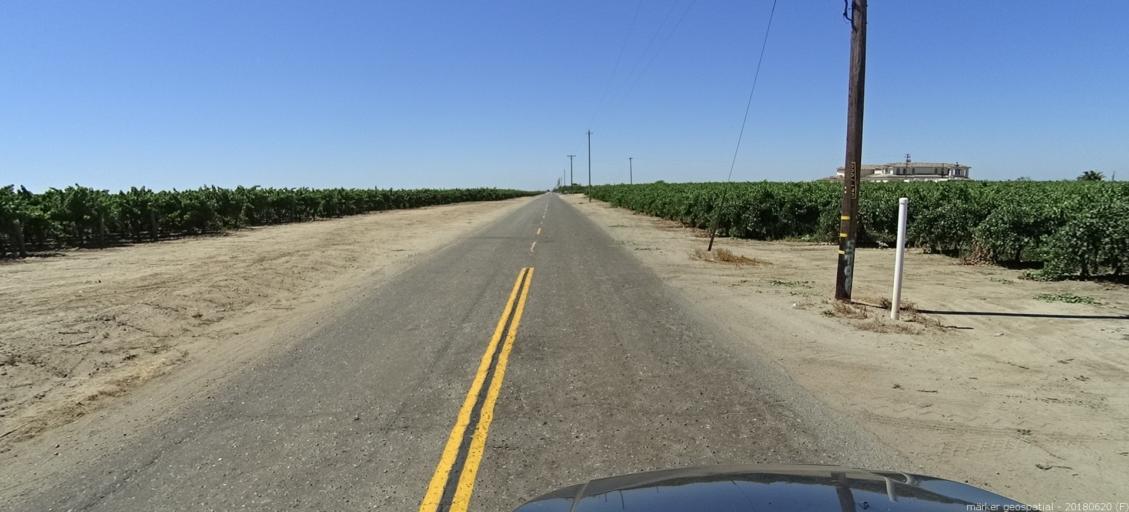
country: US
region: California
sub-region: Madera County
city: Parkwood
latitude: 36.8800
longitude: -120.0015
